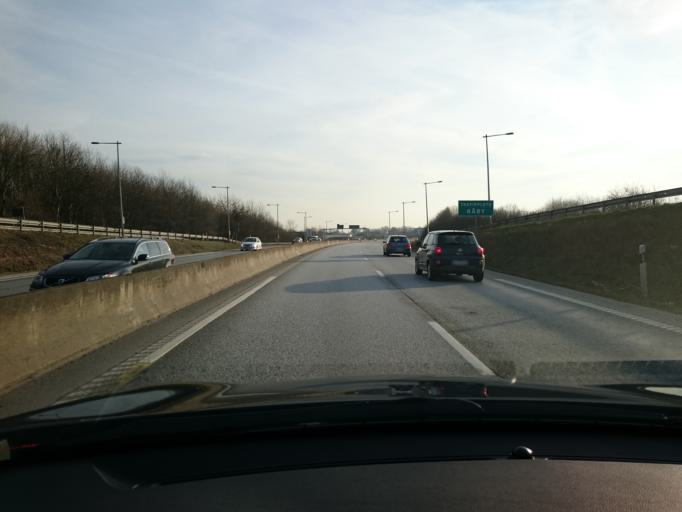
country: SE
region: Skane
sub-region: Lunds Kommun
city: Lund
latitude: 55.6973
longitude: 13.2166
